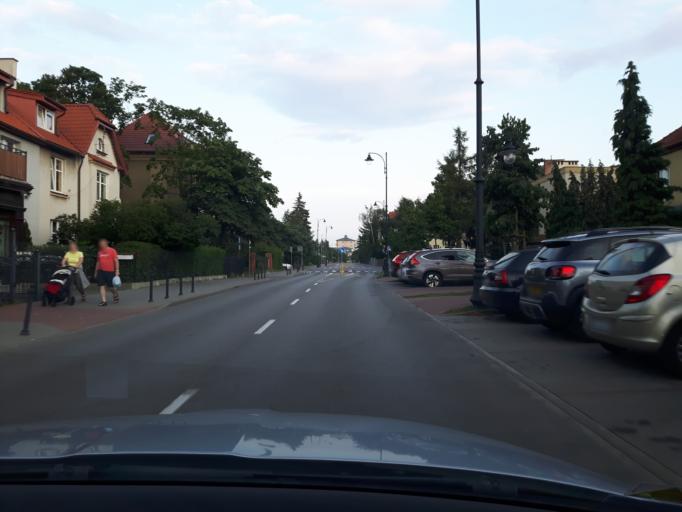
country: PL
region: Pomeranian Voivodeship
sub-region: Sopot
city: Sopot
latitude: 54.4329
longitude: 18.5717
